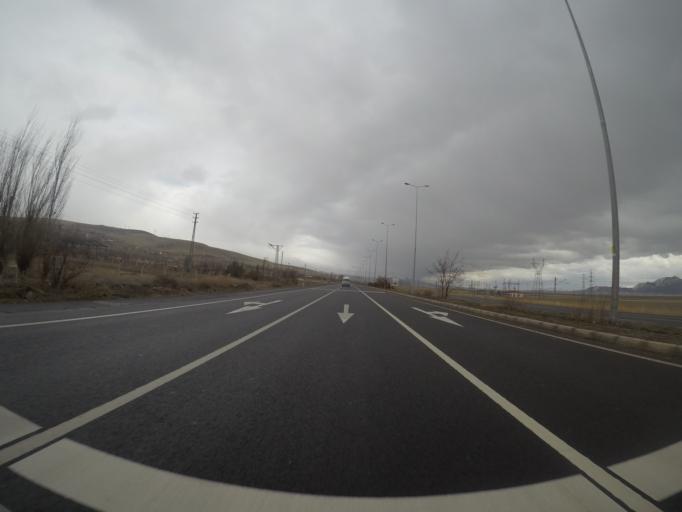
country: TR
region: Kayseri
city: Incesu
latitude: 38.7188
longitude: 35.2708
